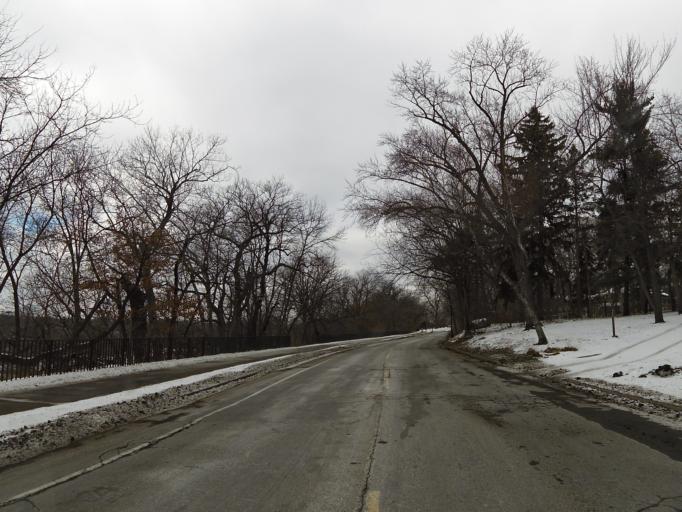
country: US
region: Minnesota
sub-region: Ramsey County
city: Lauderdale
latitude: 44.9518
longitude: -93.2019
